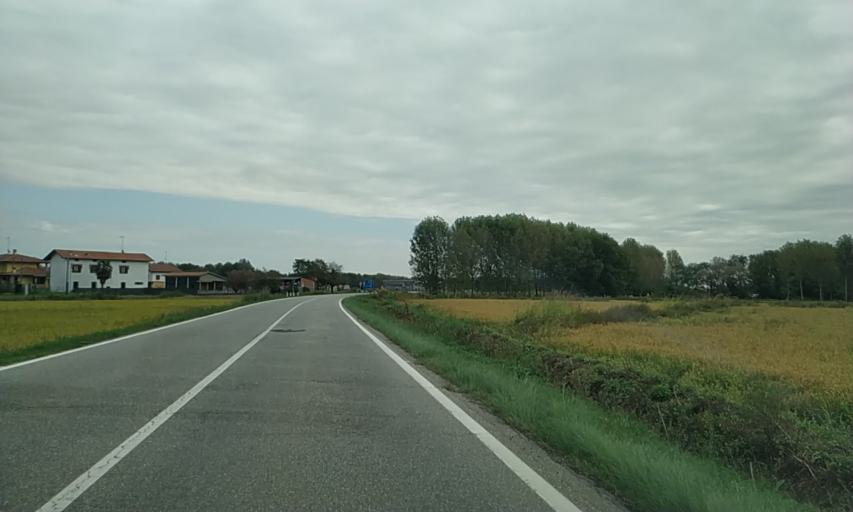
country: IT
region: Piedmont
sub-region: Provincia di Vercelli
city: Lenta
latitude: 45.5516
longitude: 8.3816
